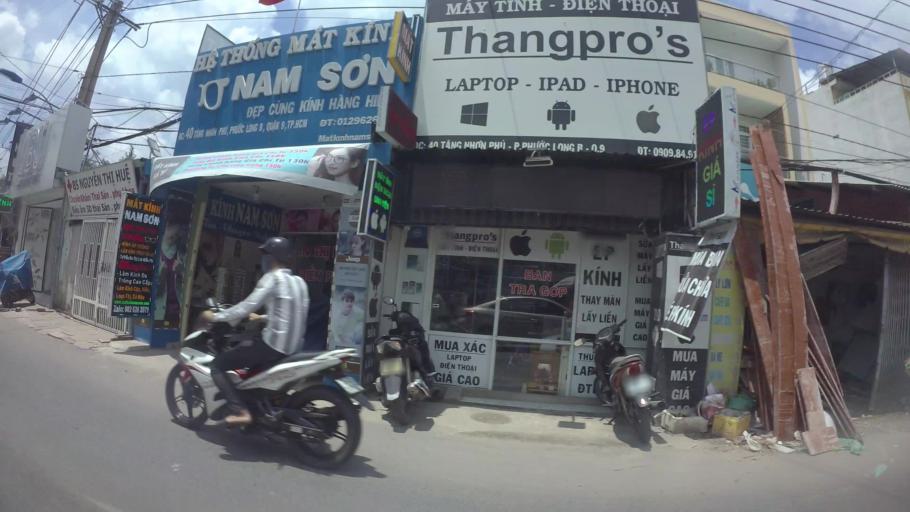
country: VN
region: Ho Chi Minh City
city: Quan Chin
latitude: 10.8310
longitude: 106.7752
